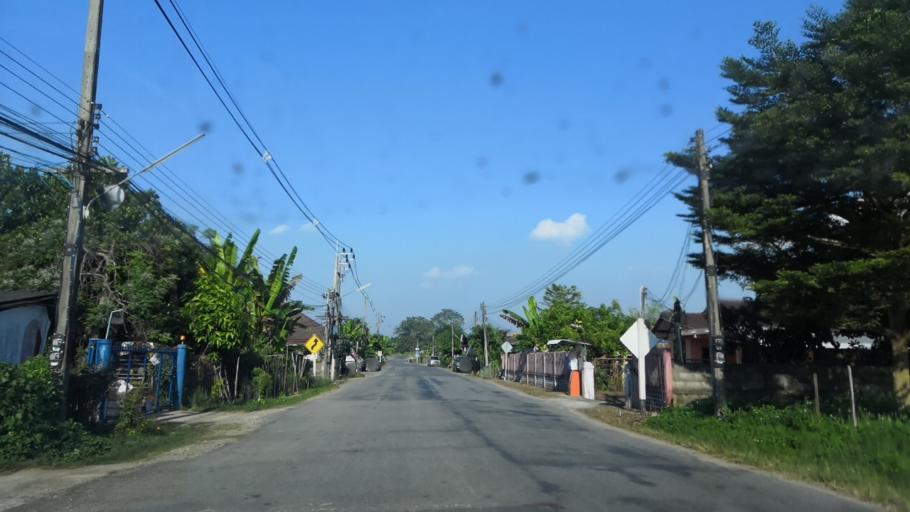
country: TH
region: Chiang Rai
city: Wiang Chai
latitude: 19.9417
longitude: 99.9151
